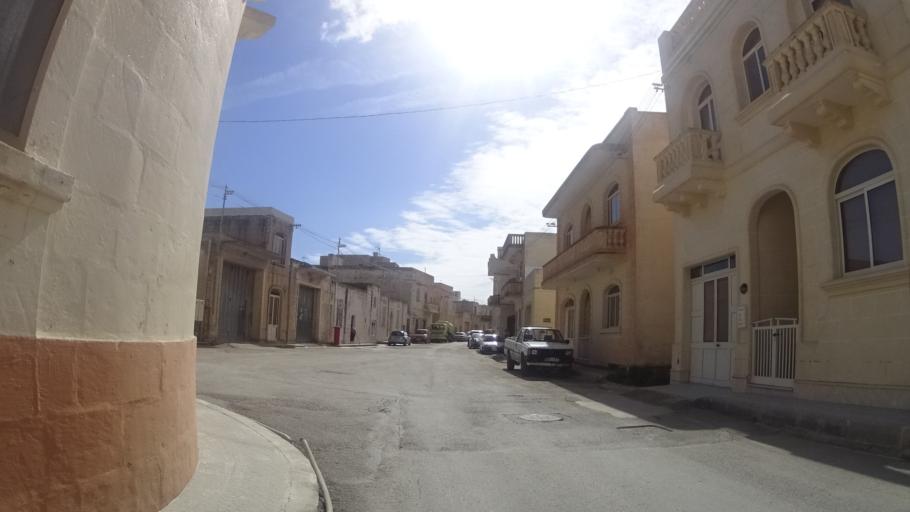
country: MT
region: In-Nadur
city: Nadur
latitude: 36.0486
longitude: 14.2999
